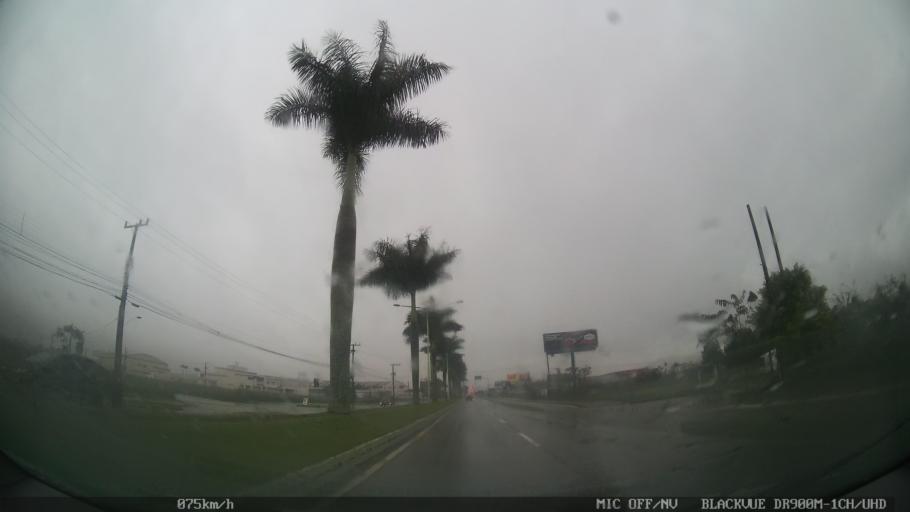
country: BR
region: Santa Catarina
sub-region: Itajai
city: Itajai
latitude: -26.9146
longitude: -48.6971
